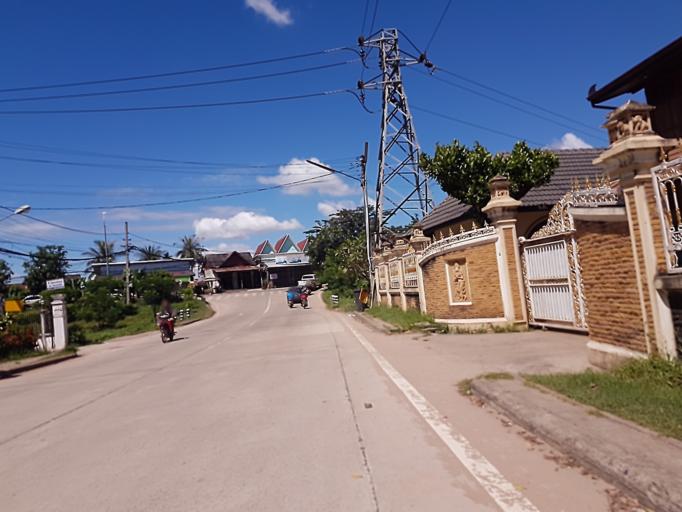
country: LA
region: Vientiane
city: Vientiane
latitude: 17.9466
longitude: 102.6232
